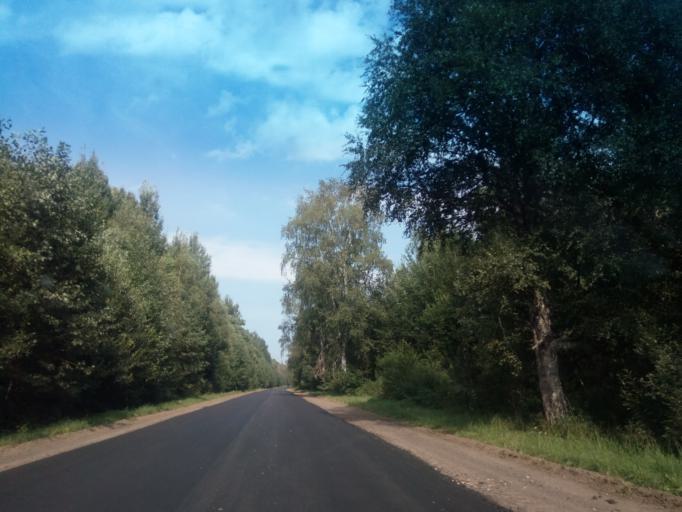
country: BY
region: Vitebsk
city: Dzisna
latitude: 55.6366
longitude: 28.3085
